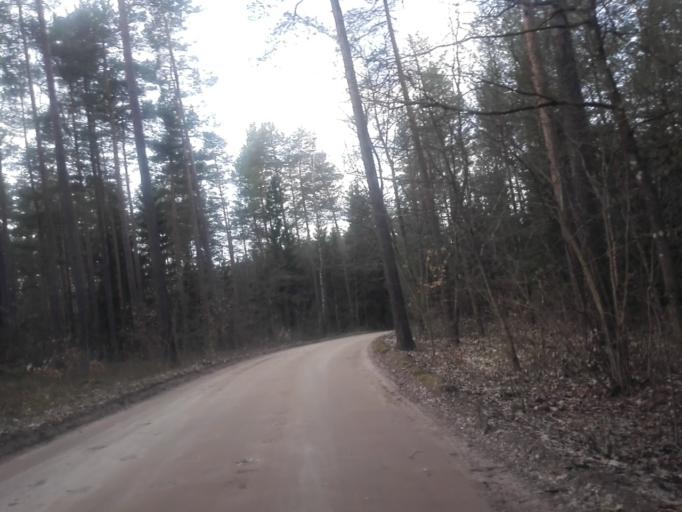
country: PL
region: Podlasie
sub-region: Powiat sejnenski
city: Sejny
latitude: 54.0233
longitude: 23.4072
